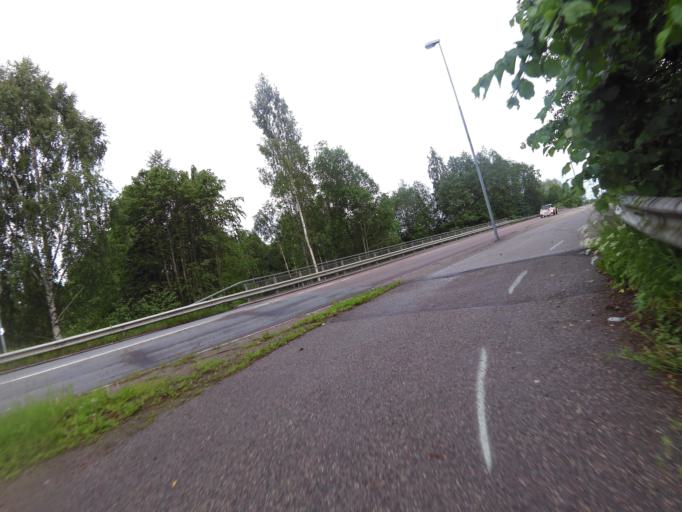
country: SE
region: Gaevleborg
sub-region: Gavle Kommun
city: Gavle
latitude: 60.6838
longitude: 17.1216
